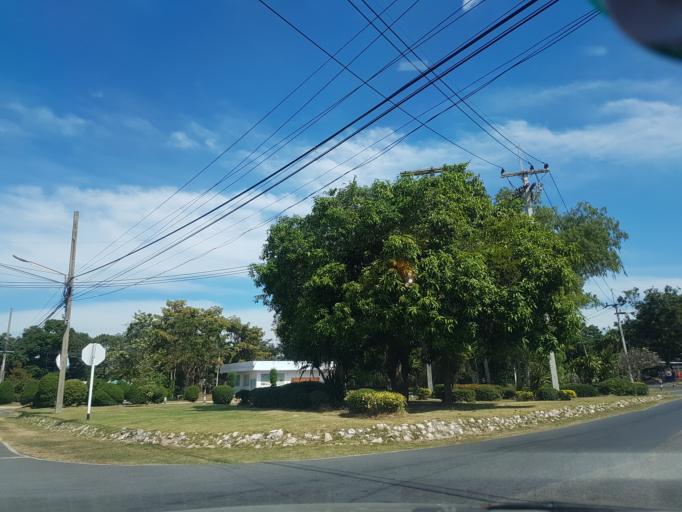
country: TH
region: Chon Buri
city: Sattahip
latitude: 12.6371
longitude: 100.9393
